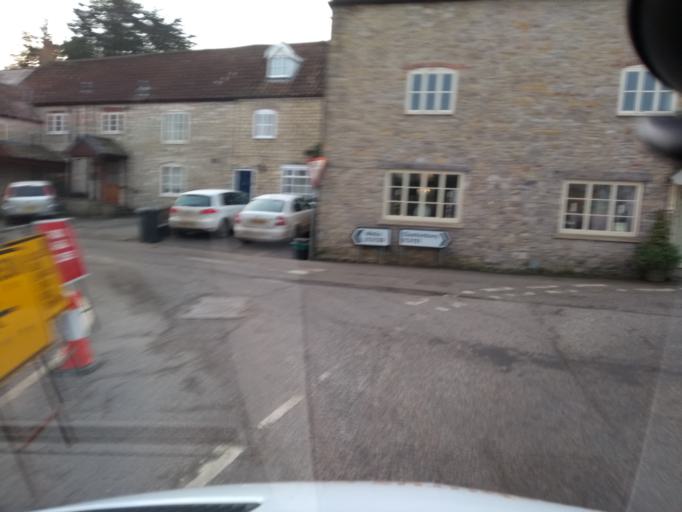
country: GB
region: England
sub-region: Somerset
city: Wedmore
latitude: 51.2266
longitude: -2.8082
